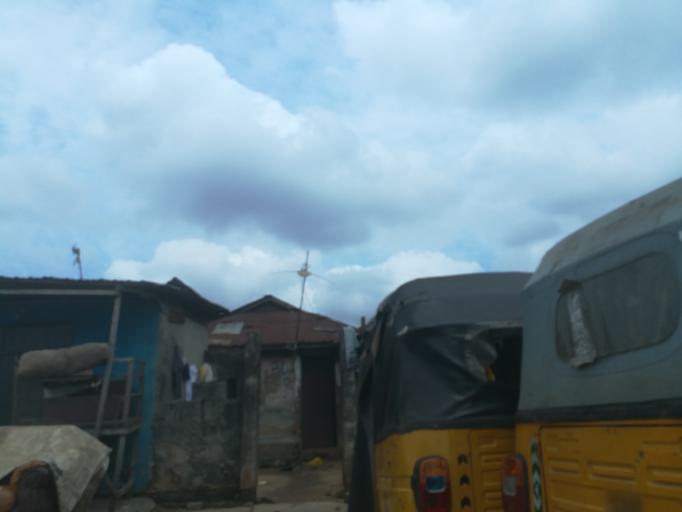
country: NG
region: Lagos
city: Somolu
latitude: 6.5446
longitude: 3.3944
